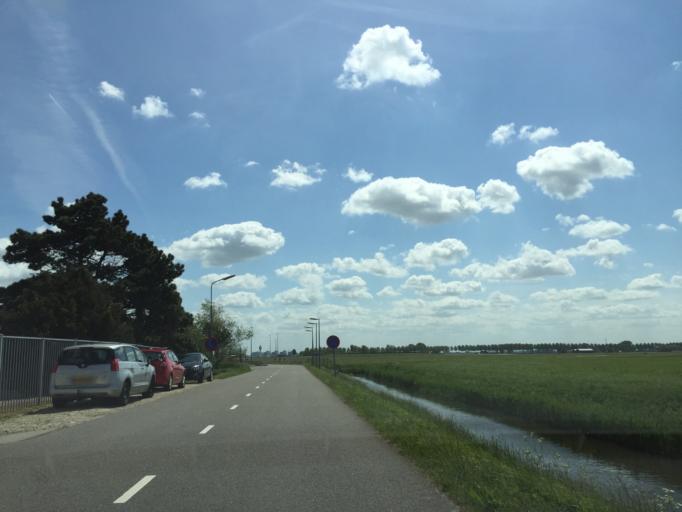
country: NL
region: North Holland
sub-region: Gemeente Haarlemmermeer
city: Hoofddorp
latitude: 52.3350
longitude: 4.7055
